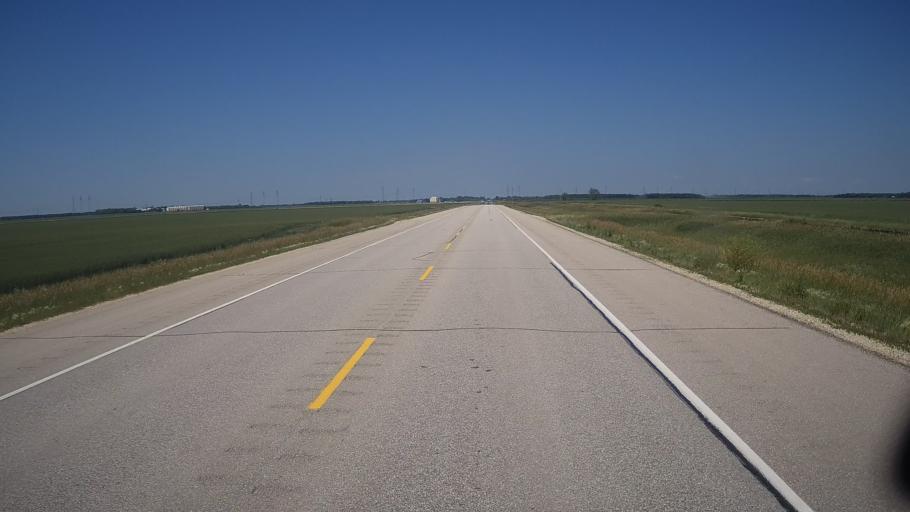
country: CA
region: Manitoba
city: Stonewall
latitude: 50.0388
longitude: -97.4035
